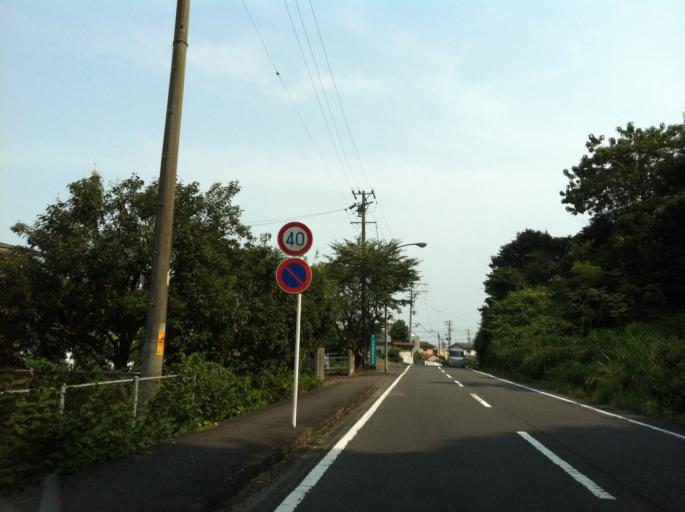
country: JP
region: Shizuoka
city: Shimada
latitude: 34.8477
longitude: 138.1811
